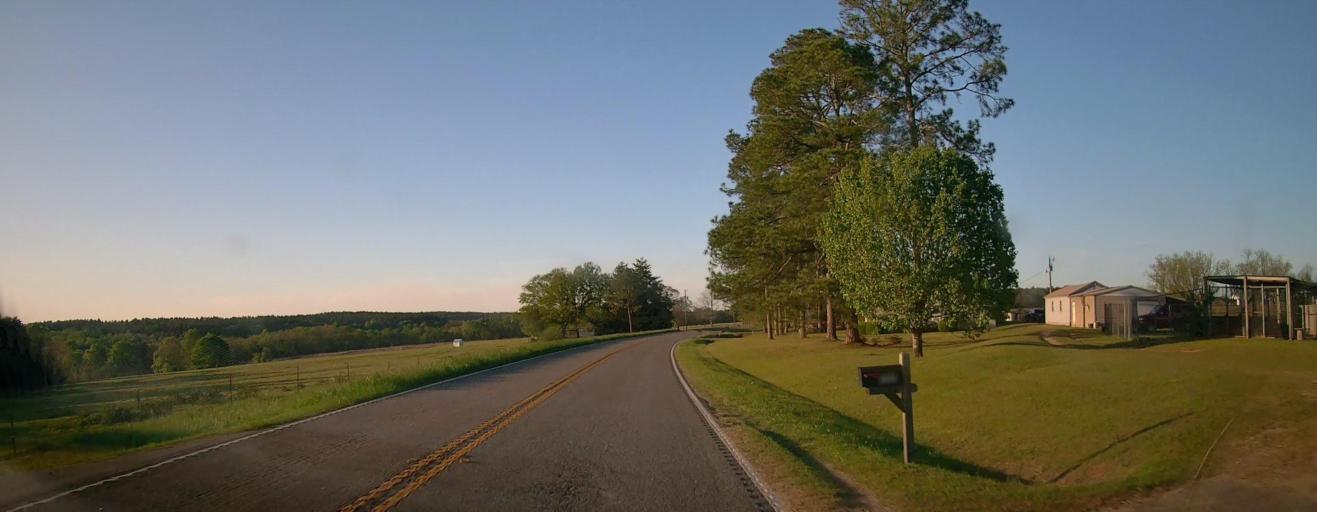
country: US
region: Georgia
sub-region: Marion County
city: Buena Vista
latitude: 32.3973
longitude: -84.4431
